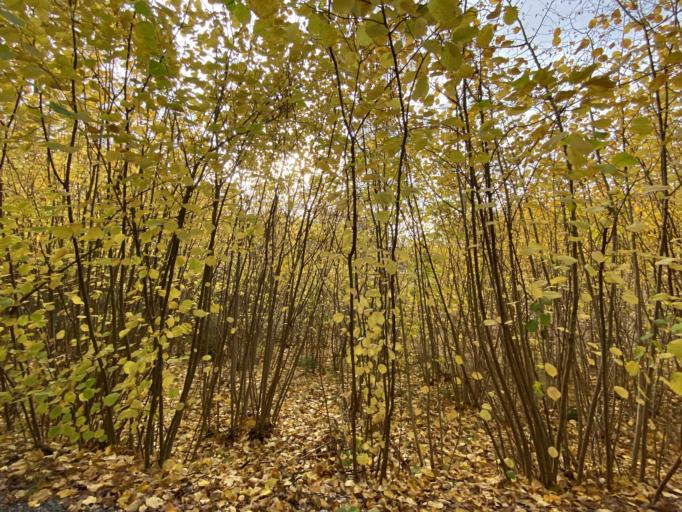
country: SE
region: Stockholm
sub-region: Salems Kommun
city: Ronninge
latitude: 59.1873
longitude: 17.7321
